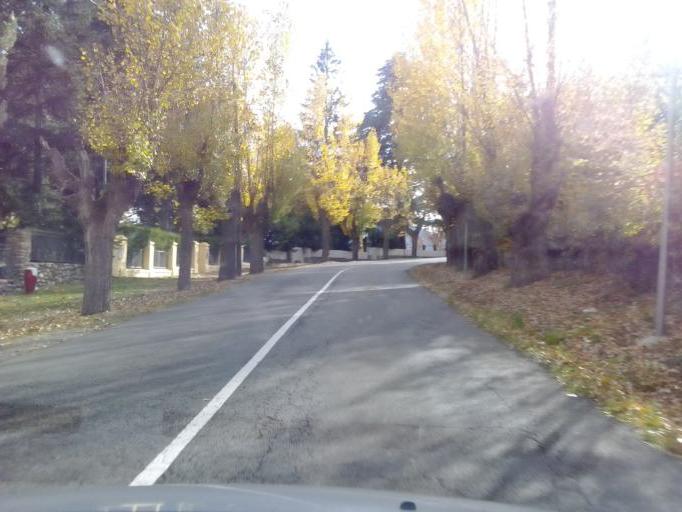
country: ES
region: Catalonia
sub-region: Provincia de Girona
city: Puigcerda
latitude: 42.4367
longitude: 1.9334
